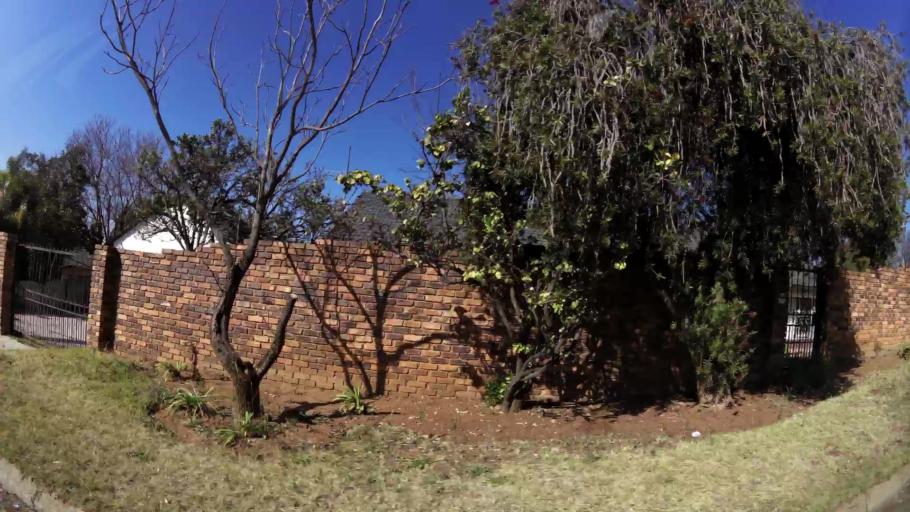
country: ZA
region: Gauteng
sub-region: Ekurhuleni Metropolitan Municipality
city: Tembisa
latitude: -26.0515
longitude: 28.2103
